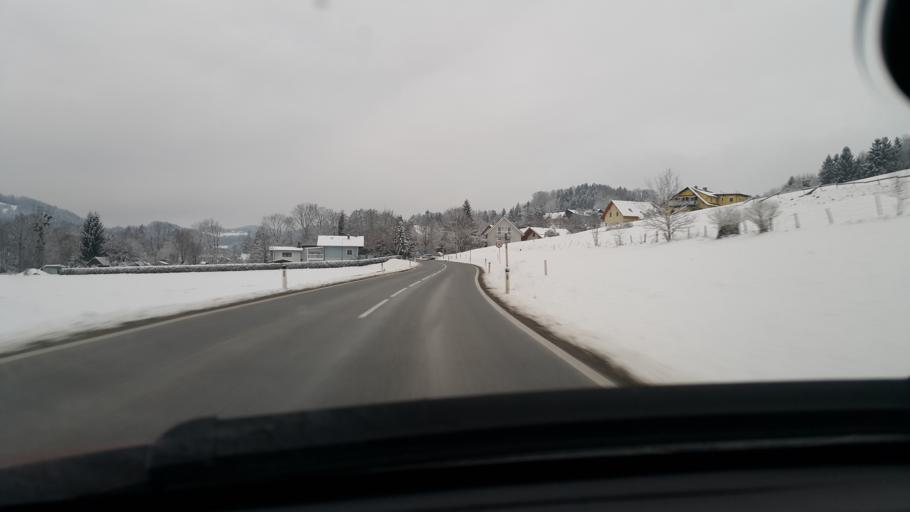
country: AT
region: Styria
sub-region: Politischer Bezirk Graz-Umgebung
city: Sankt Oswald bei Plankenwarth
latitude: 47.0702
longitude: 15.2694
